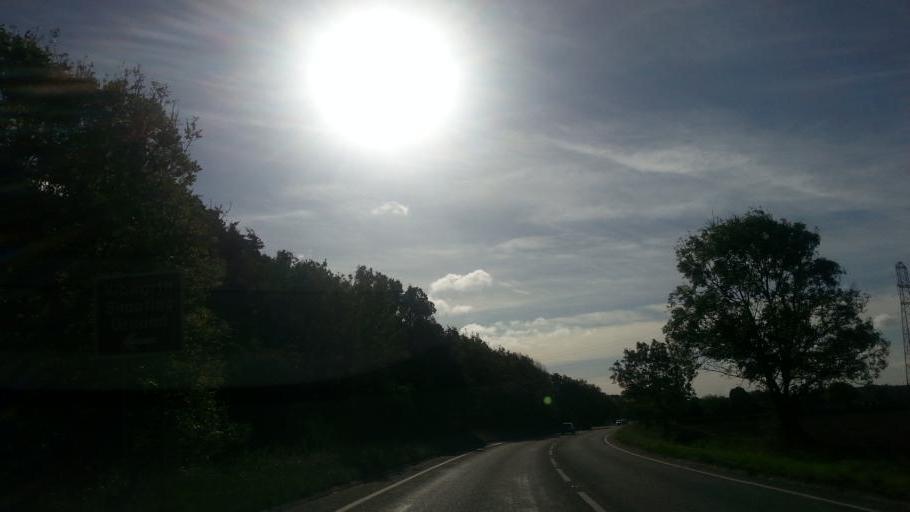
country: GB
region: England
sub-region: Leicestershire
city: Kibworth Harcourt
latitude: 52.5297
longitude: -0.9682
